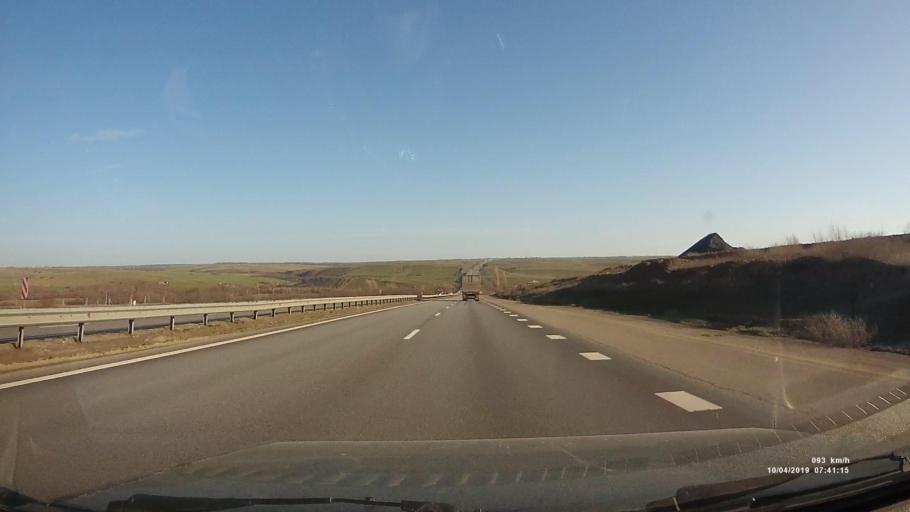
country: RU
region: Rostov
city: Likhoy
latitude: 48.1320
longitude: 40.2596
